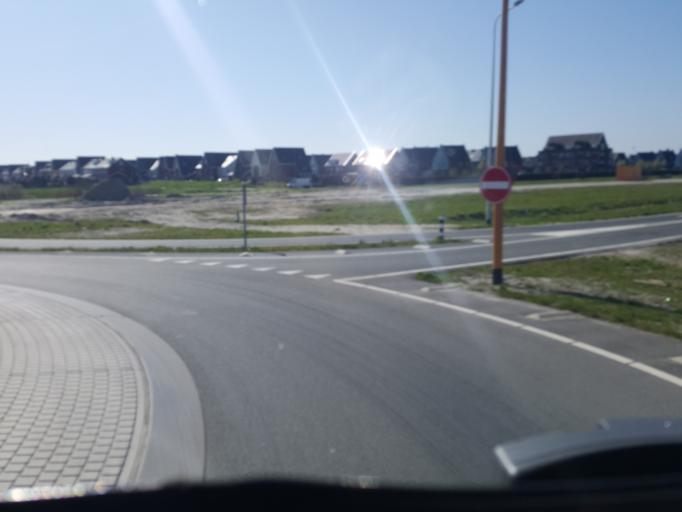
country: NL
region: North Holland
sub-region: Gemeente Hoorn
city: Hoorn
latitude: 52.6787
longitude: 5.0840
